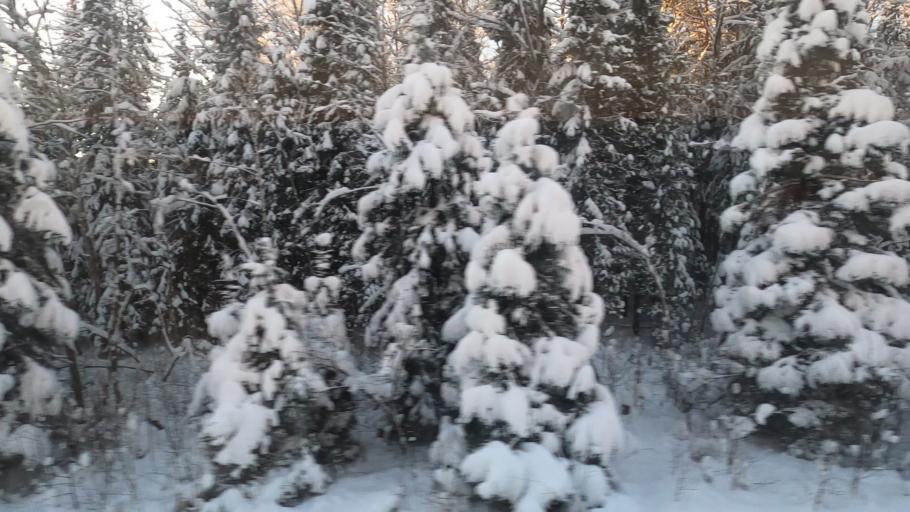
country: RU
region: Moskovskaya
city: Verbilki
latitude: 56.5261
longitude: 37.5585
